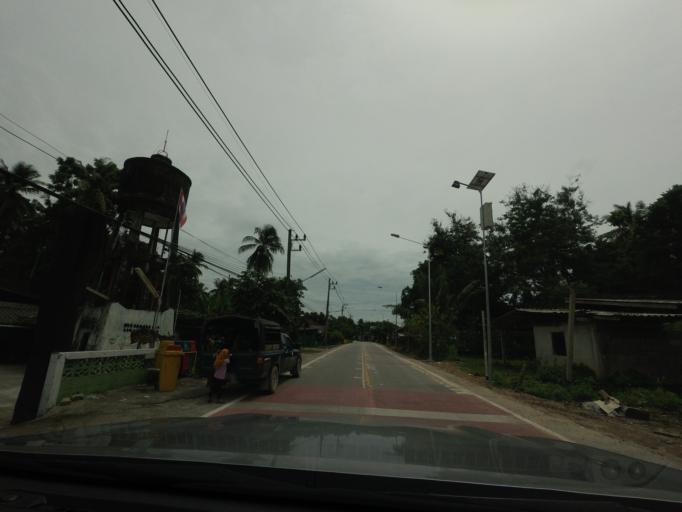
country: TH
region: Pattani
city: Kapho
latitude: 6.5791
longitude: 101.5353
